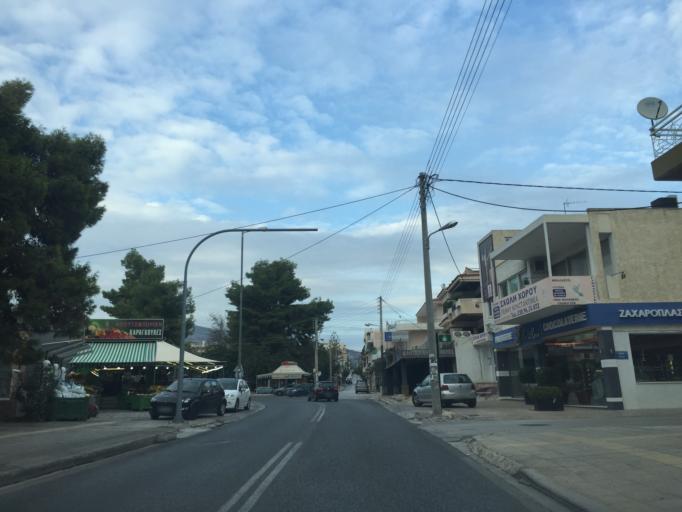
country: GR
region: Attica
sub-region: Nomarchia Anatolikis Attikis
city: Vari
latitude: 37.8300
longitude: 23.8030
